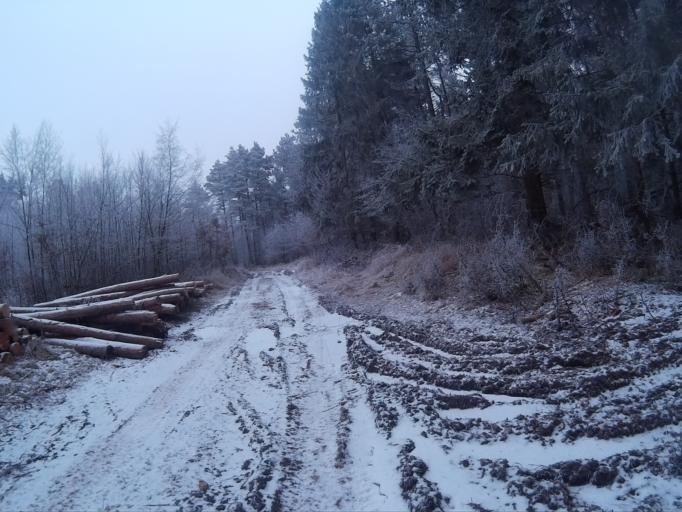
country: HU
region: Borsod-Abauj-Zemplen
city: Szendro
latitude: 48.5627
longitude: 20.6992
